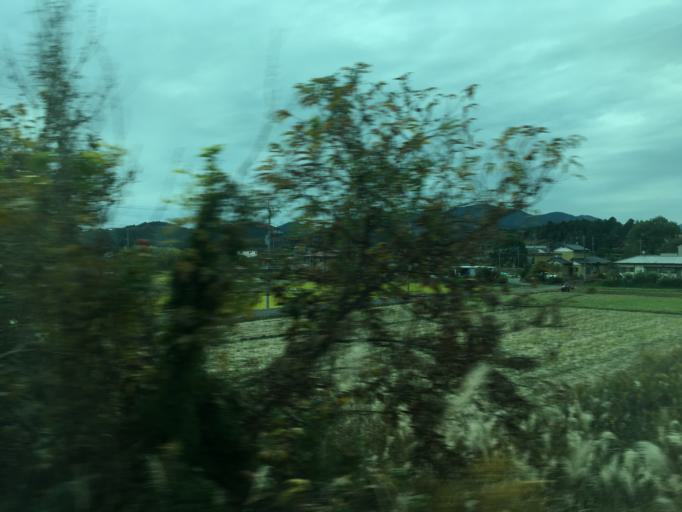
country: JP
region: Ibaraki
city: Tomobe
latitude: 36.3474
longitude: 140.2841
